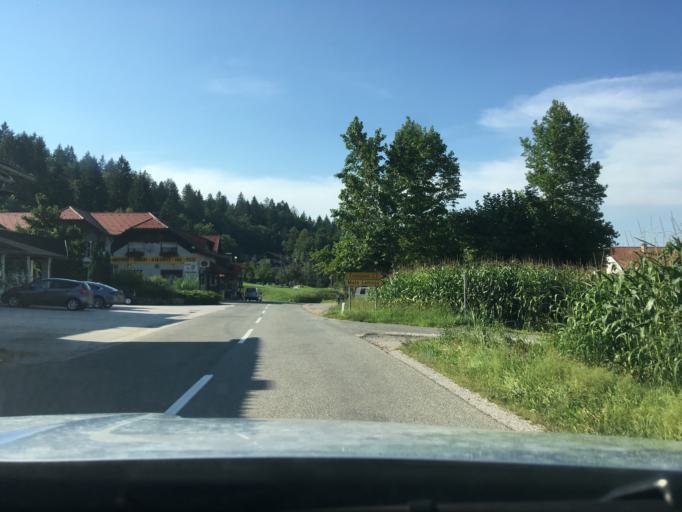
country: SI
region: Crnomelj
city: Crnomelj
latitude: 45.5014
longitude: 15.1906
